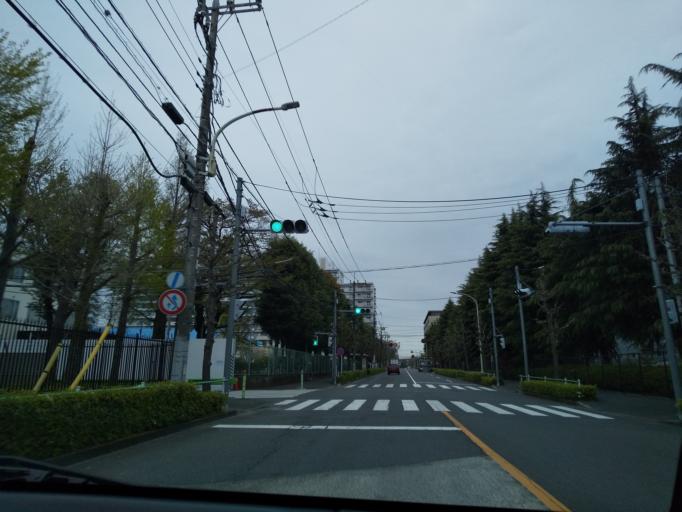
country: JP
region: Tokyo
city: Hino
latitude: 35.6547
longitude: 139.3679
